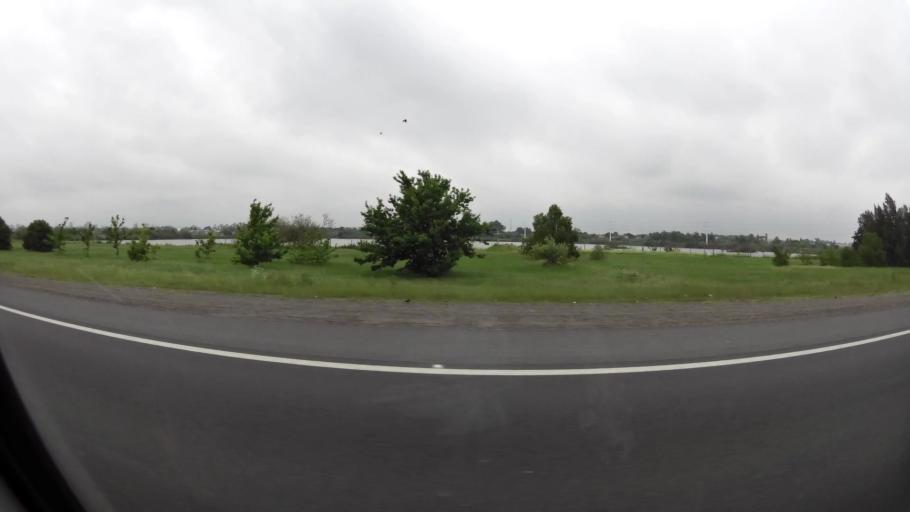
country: AR
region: Buenos Aires
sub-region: Partido de Quilmes
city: Quilmes
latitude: -34.7343
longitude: -58.2147
